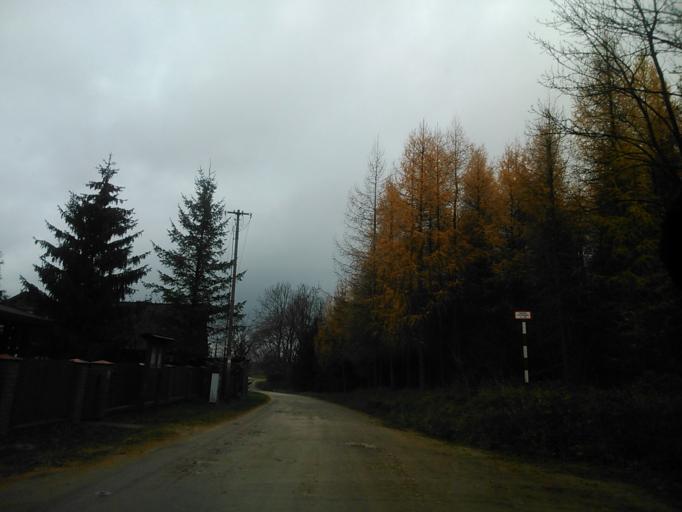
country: PL
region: Kujawsko-Pomorskie
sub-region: Powiat golubsko-dobrzynski
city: Radomin
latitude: 53.1345
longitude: 19.1698
